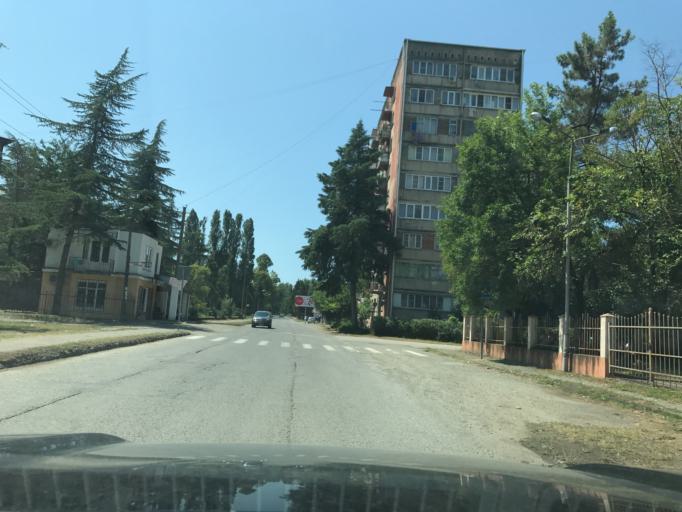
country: GE
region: Abkhazia
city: Bich'vinta
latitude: 43.1626
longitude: 40.3373
